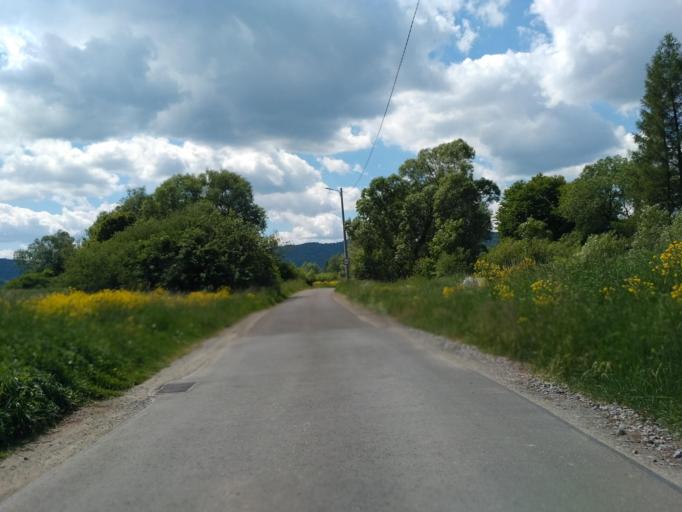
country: PL
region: Subcarpathian Voivodeship
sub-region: Powiat krosnienski
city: Dukla
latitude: 49.5619
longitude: 21.6948
